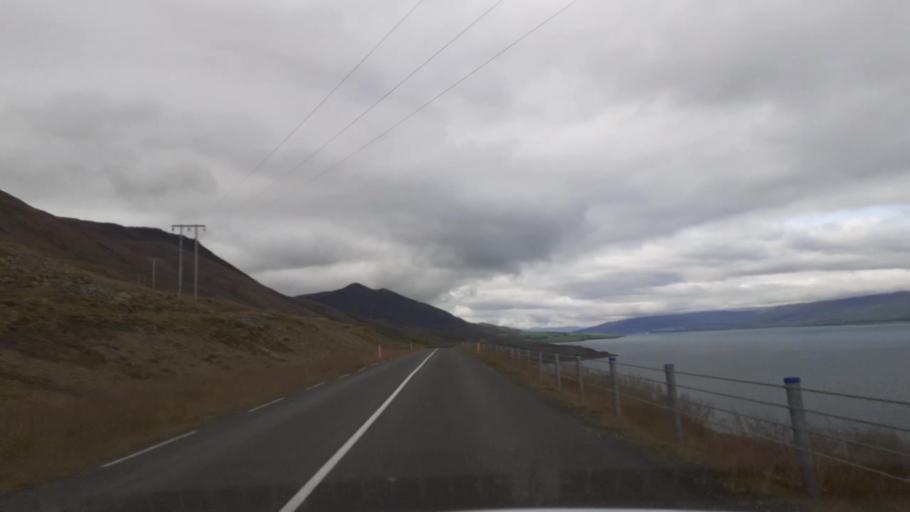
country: IS
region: Northeast
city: Akureyri
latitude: 65.8528
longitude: -18.0608
